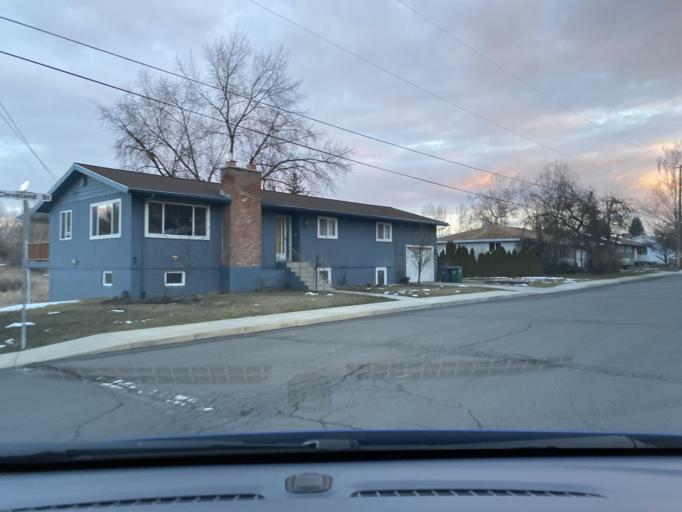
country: US
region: Idaho
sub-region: Latah County
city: Moscow
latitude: 46.7425
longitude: -116.9832
